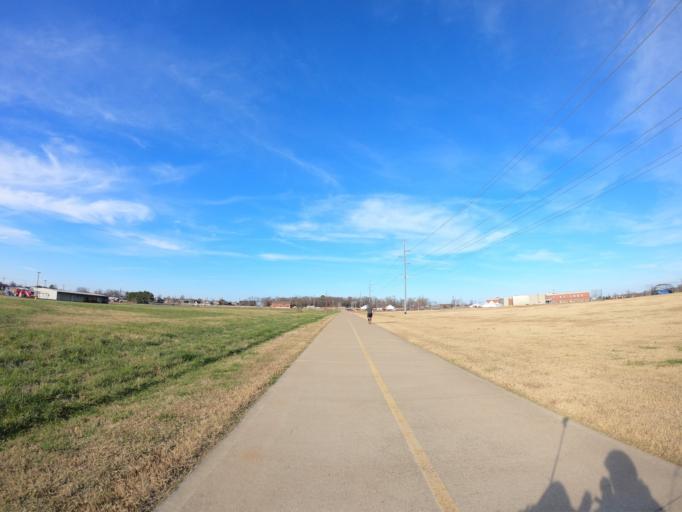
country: US
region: Arkansas
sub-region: Benton County
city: Lowell
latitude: 36.2771
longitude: -94.1698
